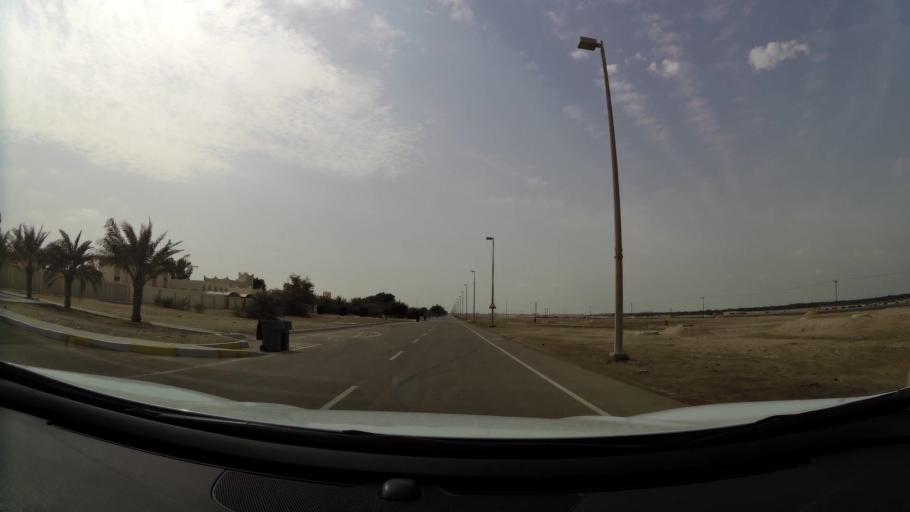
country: AE
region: Abu Dhabi
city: Abu Dhabi
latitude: 24.5748
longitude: 54.6426
